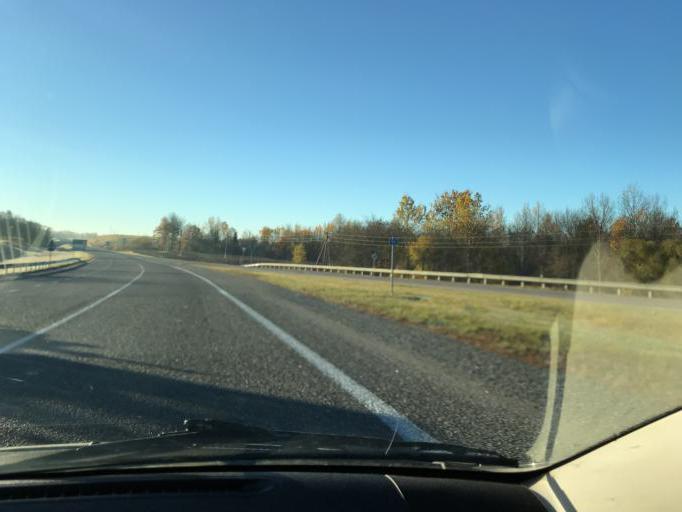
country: BY
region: Vitebsk
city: Vitebsk
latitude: 55.0985
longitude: 30.2999
